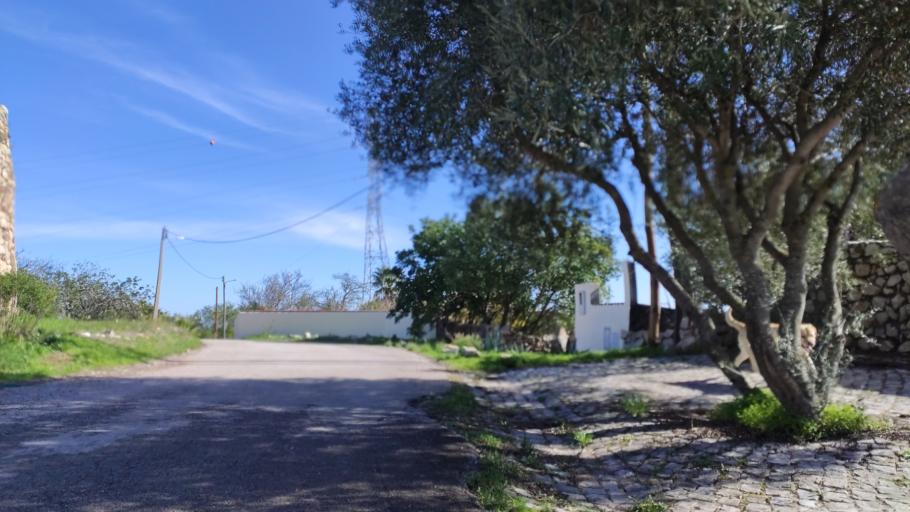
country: PT
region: Faro
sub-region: Sao Bras de Alportel
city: Sao Bras de Alportel
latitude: 37.1517
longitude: -7.8620
